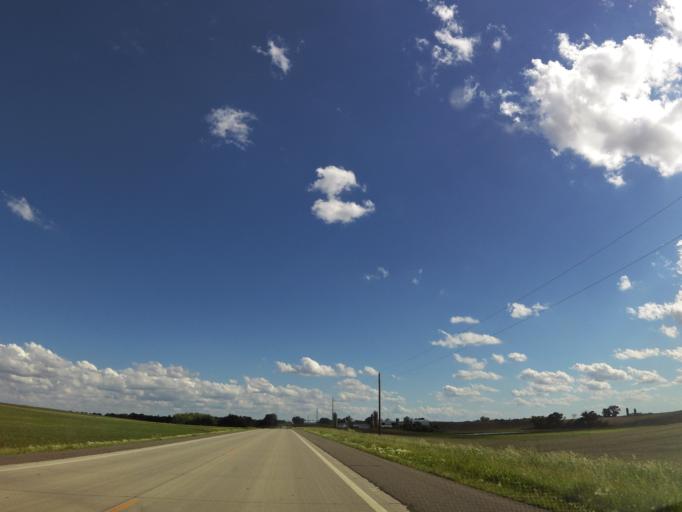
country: US
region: Minnesota
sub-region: Wright County
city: Cokato
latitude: 44.9881
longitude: -94.1754
